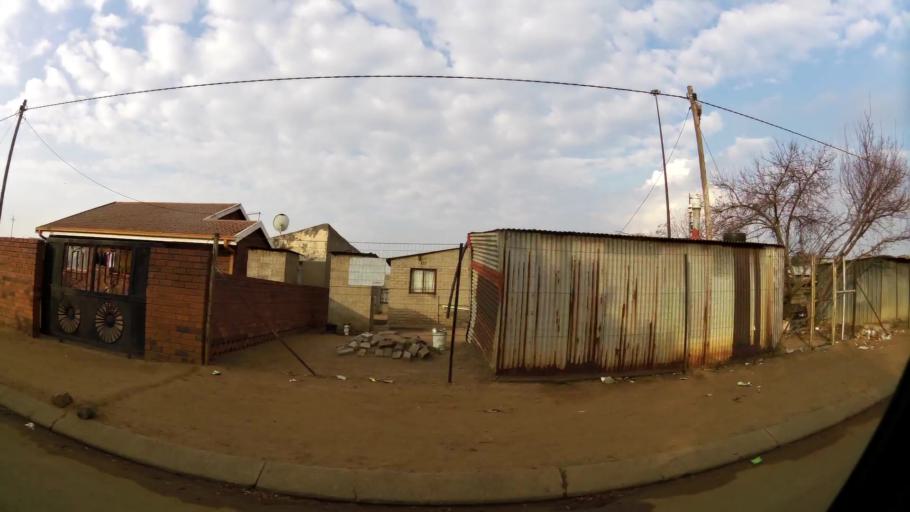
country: ZA
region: Gauteng
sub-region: Sedibeng District Municipality
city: Vanderbijlpark
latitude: -26.6779
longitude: 27.8690
